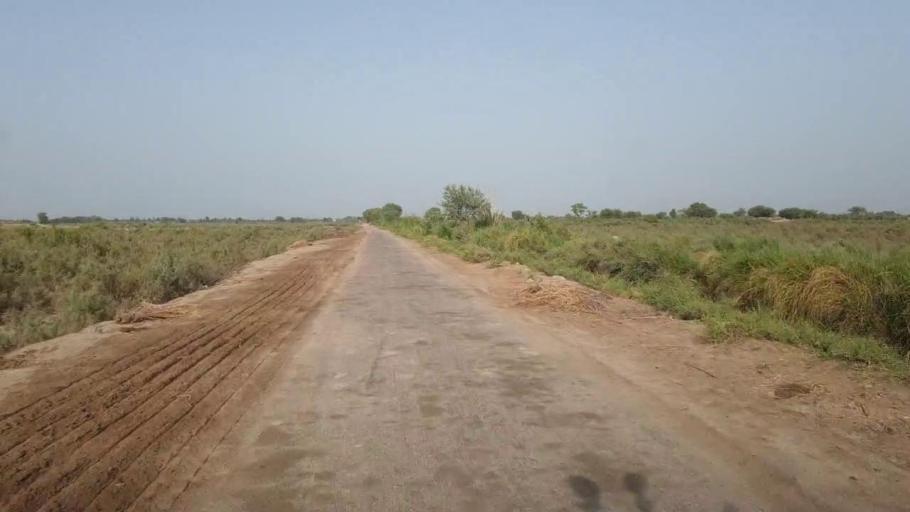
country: PK
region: Sindh
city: Daur
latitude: 26.3400
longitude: 68.2356
